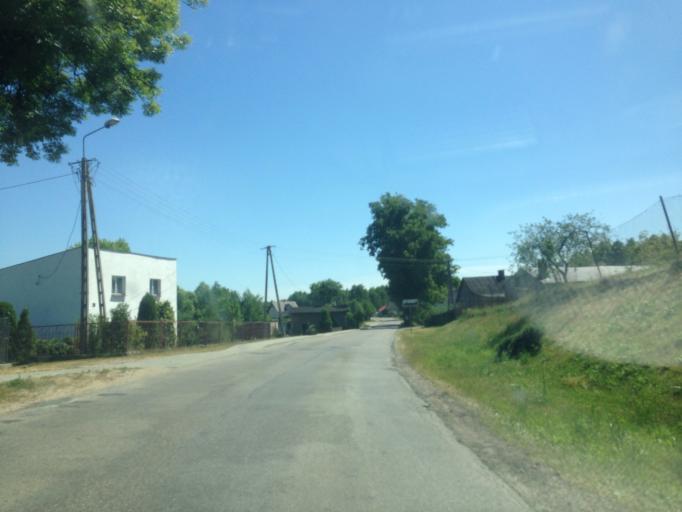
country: PL
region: Kujawsko-Pomorskie
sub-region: Powiat brodnicki
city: Bartniczka
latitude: 53.2435
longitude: 19.6130
